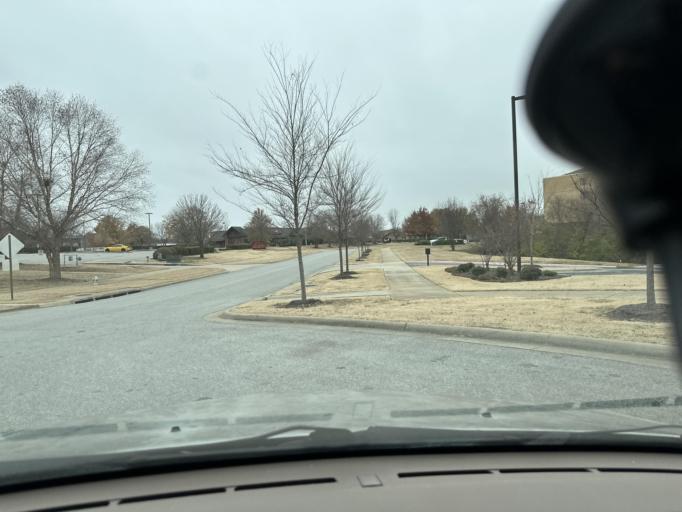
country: US
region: Arkansas
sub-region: Washington County
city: Johnson
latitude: 36.1186
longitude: -94.1479
